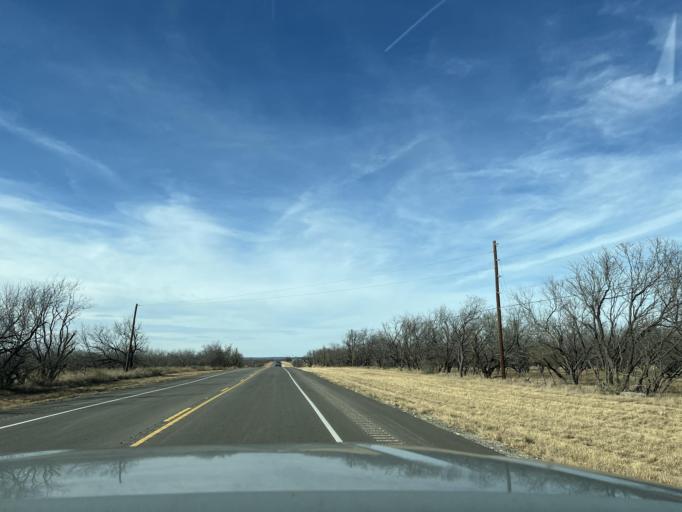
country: US
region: Texas
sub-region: Shackelford County
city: Albany
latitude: 32.5931
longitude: -99.1914
